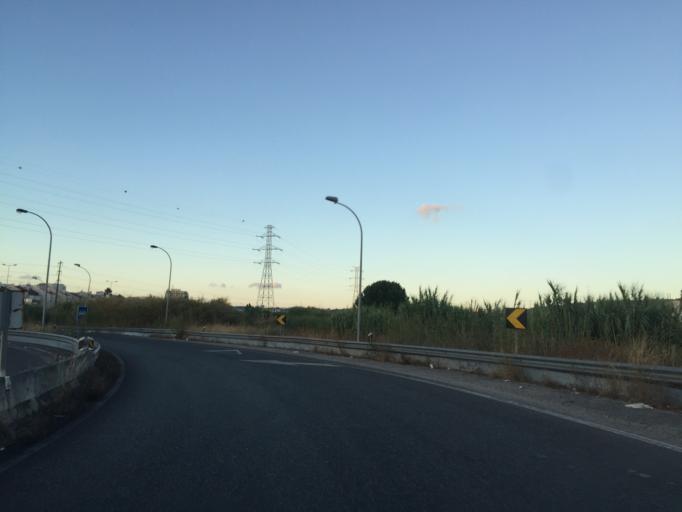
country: PT
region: Lisbon
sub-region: Odivelas
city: Odivelas
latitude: 38.7801
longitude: -9.1886
